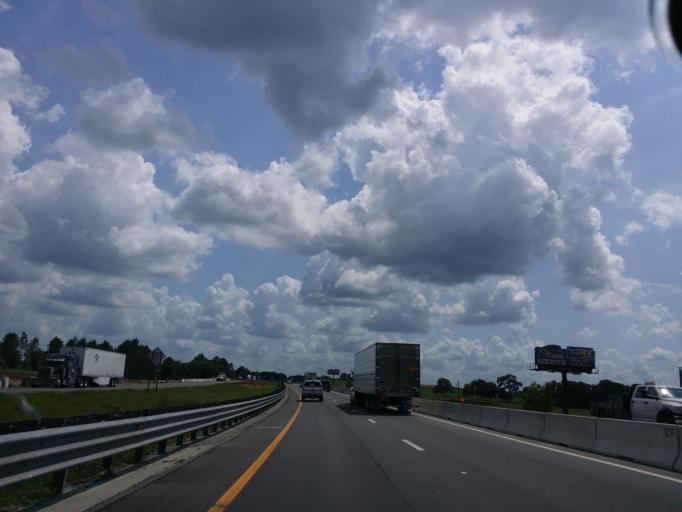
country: US
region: Florida
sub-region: Hernando County
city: Hill 'n Dale
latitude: 28.4965
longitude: -82.2485
